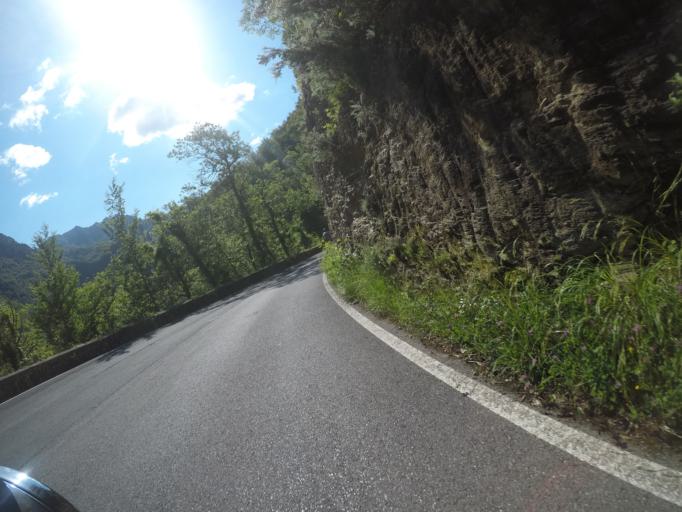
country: IT
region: Tuscany
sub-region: Provincia di Massa-Carrara
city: Montignoso
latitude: 44.0525
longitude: 10.1796
